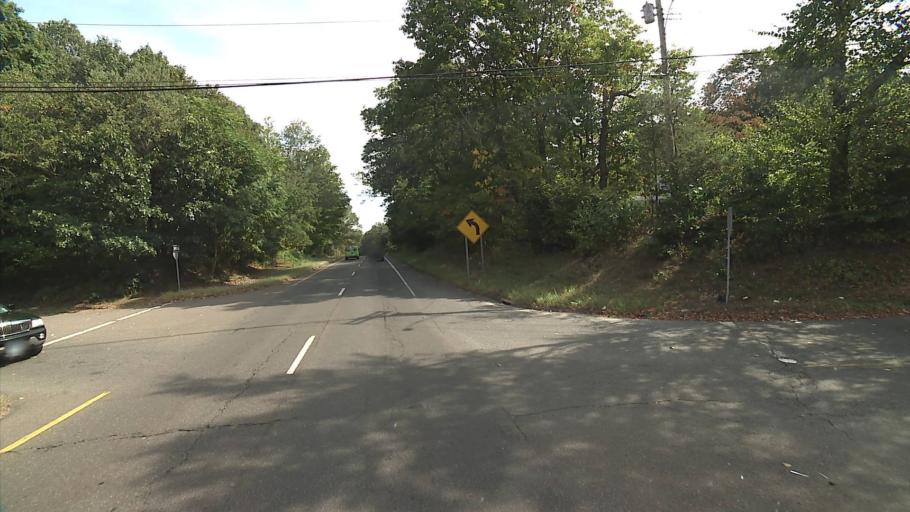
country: US
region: Connecticut
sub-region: New Haven County
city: Orange
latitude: 41.2994
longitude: -72.9927
